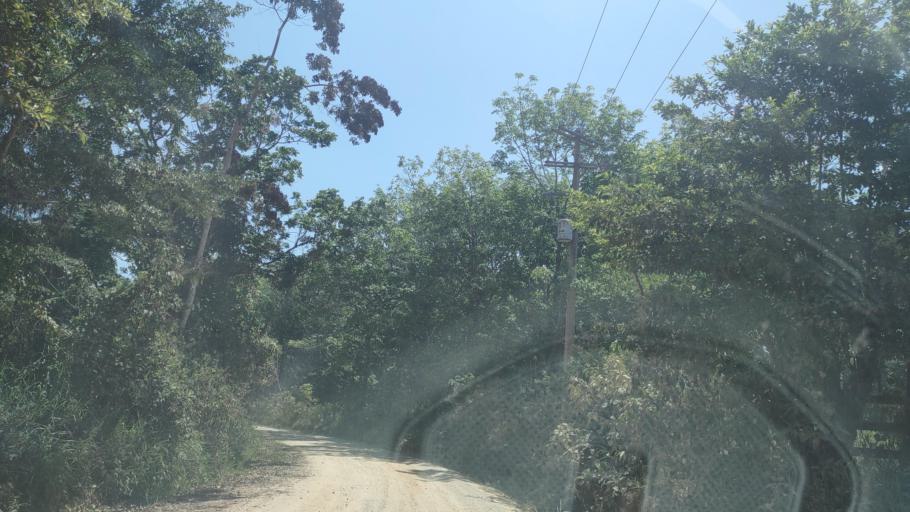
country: MX
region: Veracruz
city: Las Choapas
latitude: 17.7694
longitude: -94.1528
